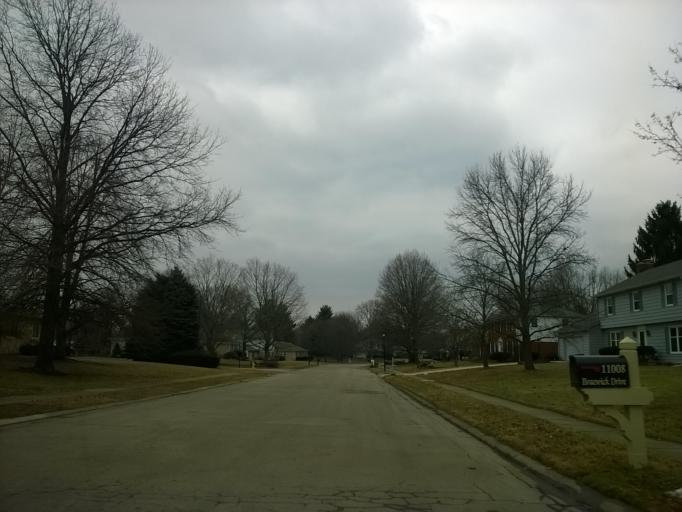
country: US
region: Indiana
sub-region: Hamilton County
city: Carmel
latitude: 39.9473
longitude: -86.1024
